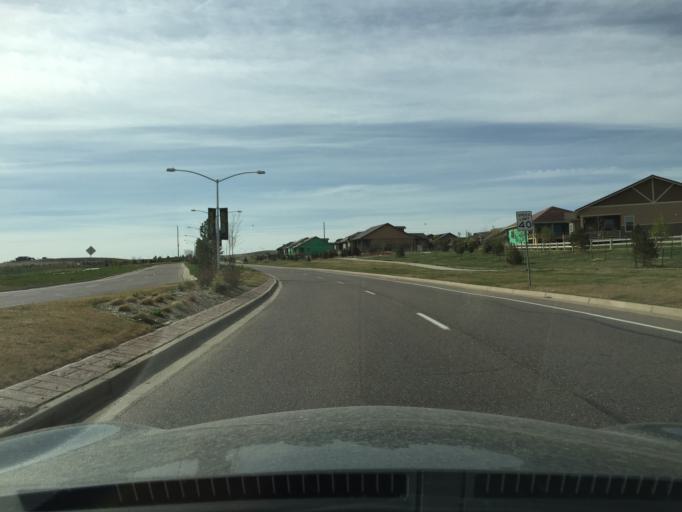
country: US
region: Colorado
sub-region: Boulder County
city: Lafayette
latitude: 39.9868
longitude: -105.0388
